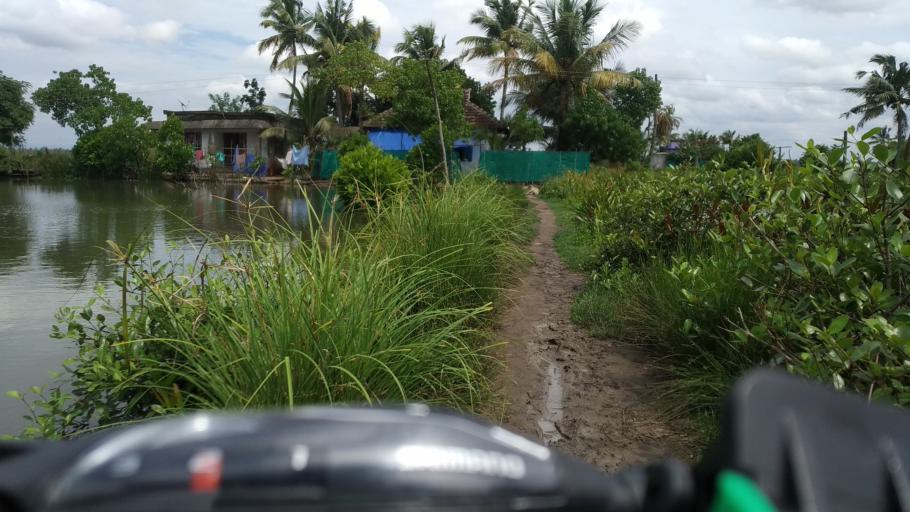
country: IN
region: Kerala
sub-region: Ernakulam
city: Elur
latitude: 10.0825
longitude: 76.2224
